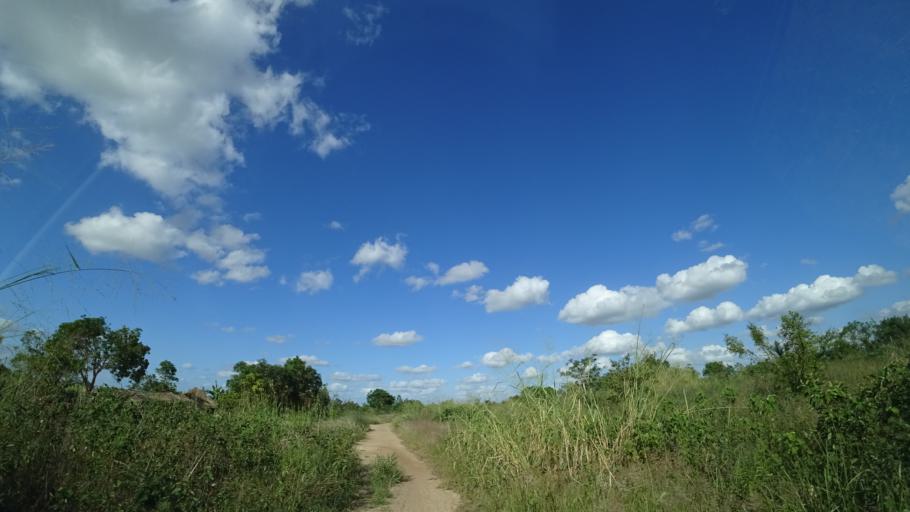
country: MZ
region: Sofala
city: Dondo
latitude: -19.4303
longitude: 34.7269
